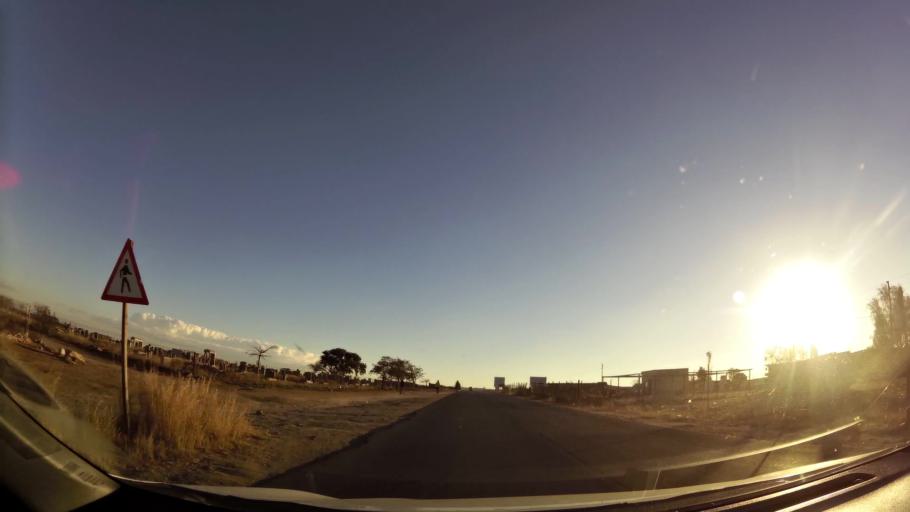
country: ZA
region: Limpopo
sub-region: Capricorn District Municipality
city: Polokwane
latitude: -23.8362
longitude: 29.3617
